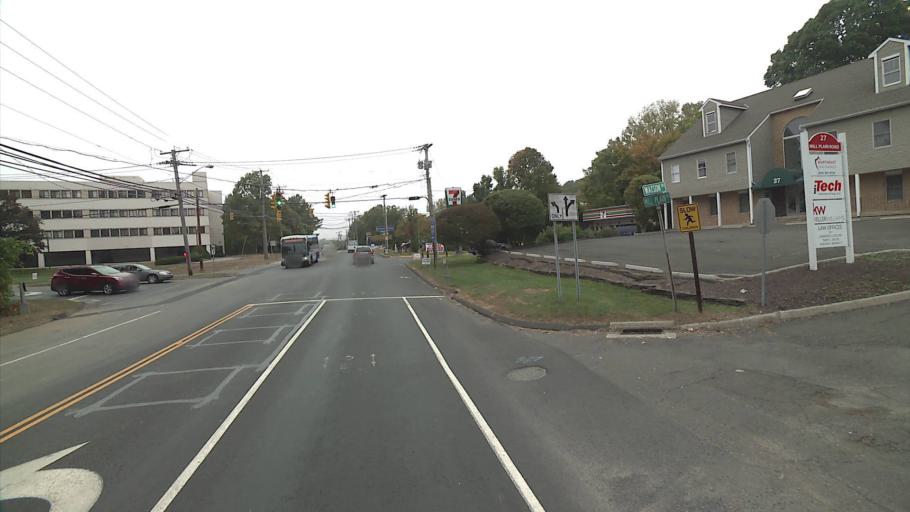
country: US
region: Connecticut
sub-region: Fairfield County
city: Danbury
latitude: 41.3886
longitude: -73.4965
